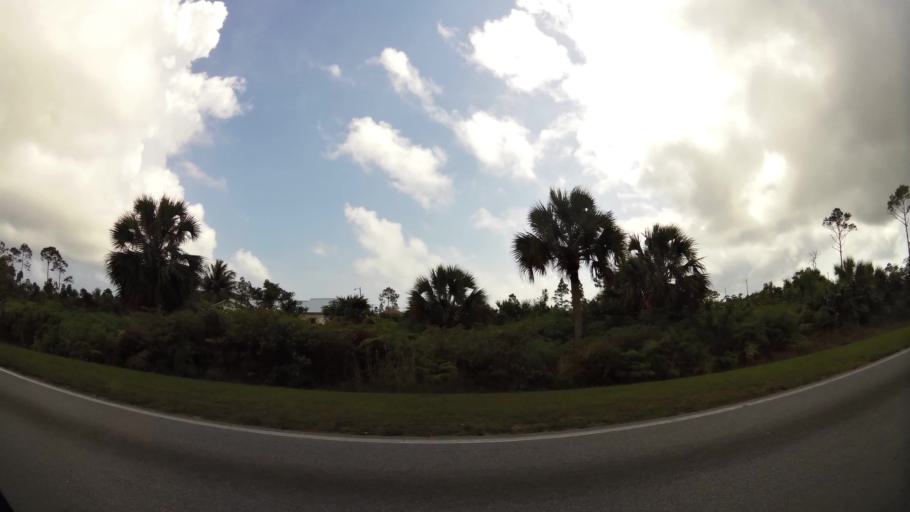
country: BS
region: Freeport
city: Freeport
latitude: 26.5172
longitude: -78.7155
